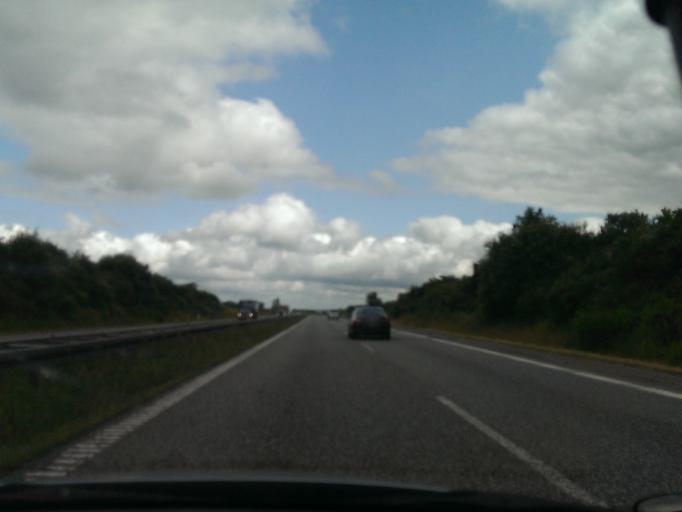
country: DK
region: North Denmark
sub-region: Mariagerfjord Kommune
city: Hobro
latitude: 56.6580
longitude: 9.7364
